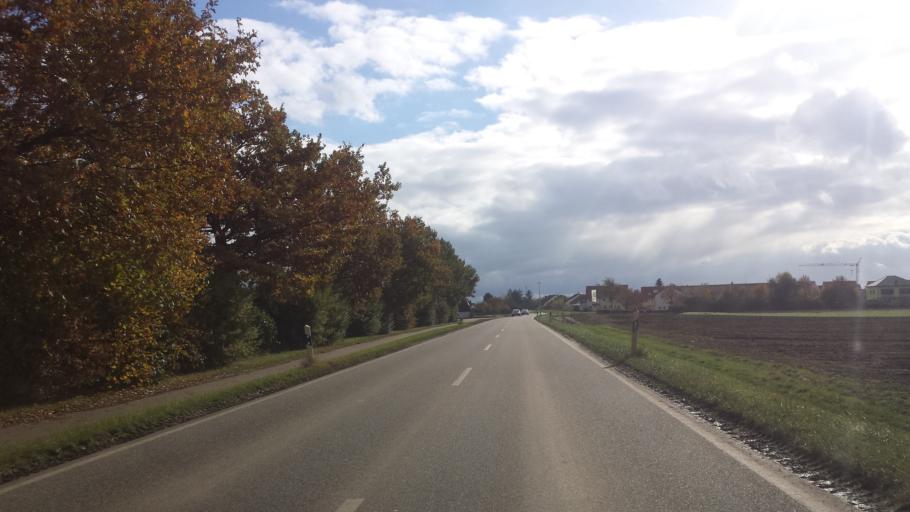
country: DE
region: Rheinland-Pfalz
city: Dannstadt-Schauernheim
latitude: 49.4443
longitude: 8.2982
